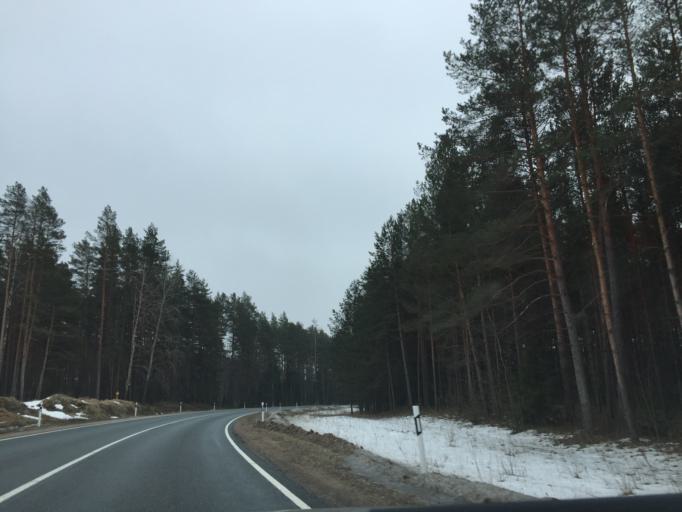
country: LV
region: Olaine
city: Olaine
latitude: 56.6228
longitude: 24.0116
